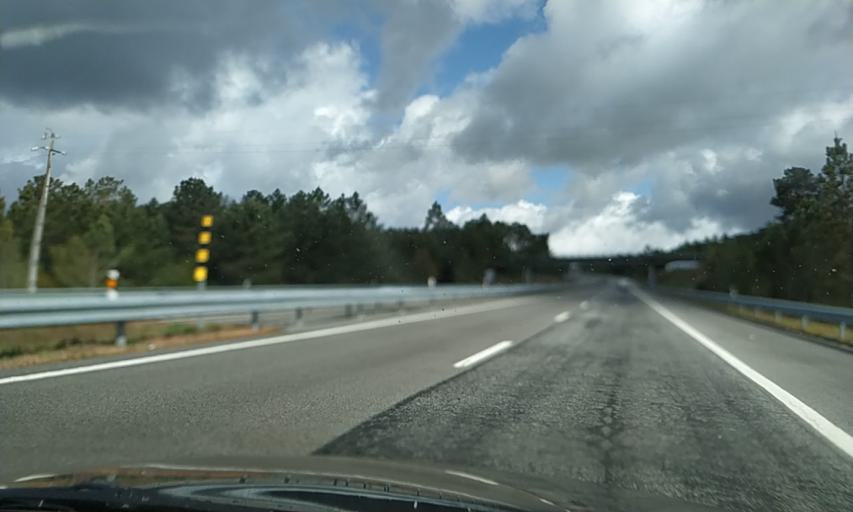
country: PT
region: Viseu
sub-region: Castro Daire
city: Castro Daire
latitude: 40.8483
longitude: -7.9272
